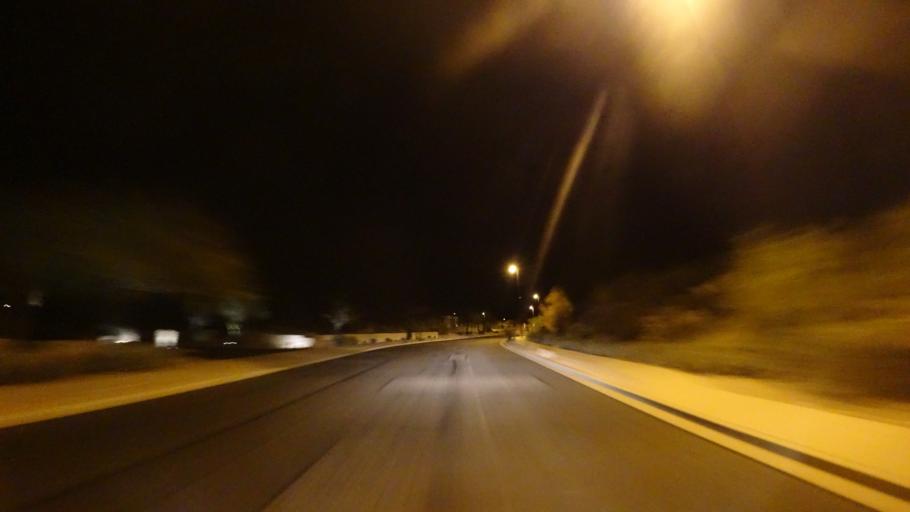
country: US
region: Arizona
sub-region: Maricopa County
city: Fountain Hills
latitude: 33.4937
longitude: -111.6950
